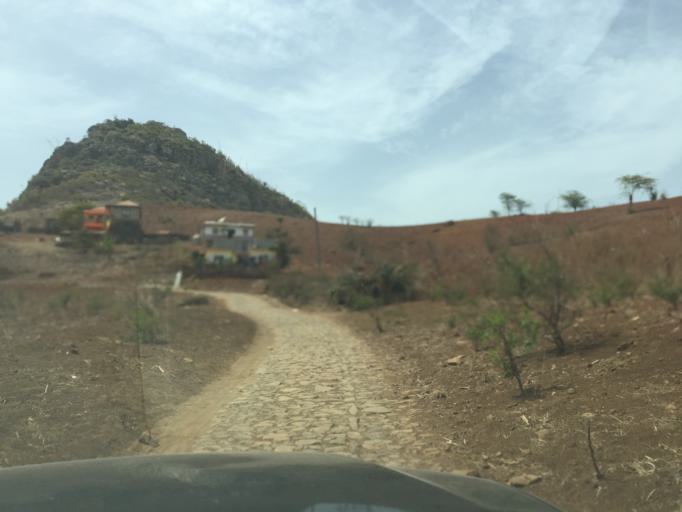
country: CV
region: Santa Catarina
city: Assomada
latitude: 15.1138
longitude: -23.6540
